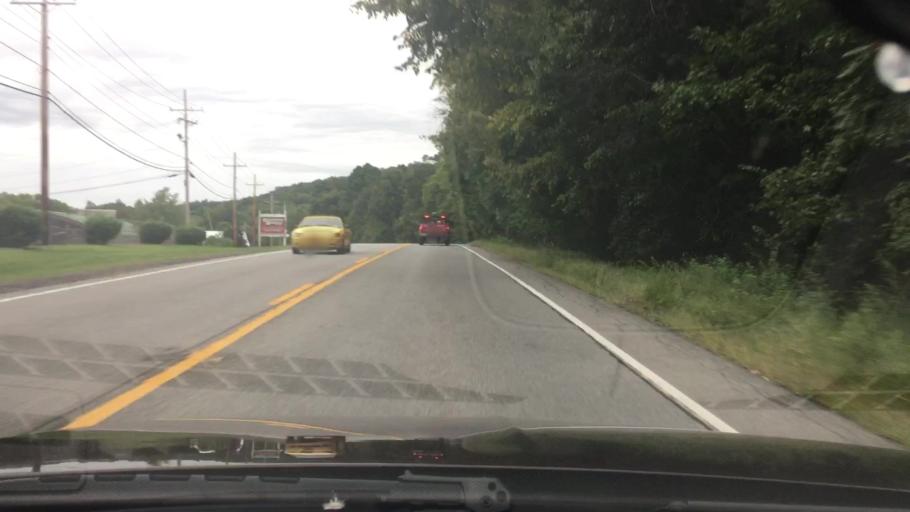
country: US
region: New York
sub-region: Dutchess County
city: Millbrook
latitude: 41.7809
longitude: -73.7619
